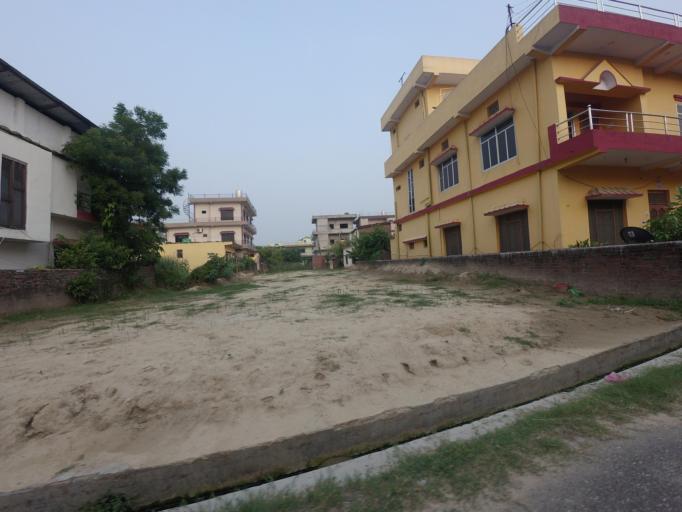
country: NP
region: Western Region
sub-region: Lumbini Zone
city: Bhairahawa
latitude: 27.5132
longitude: 83.4466
